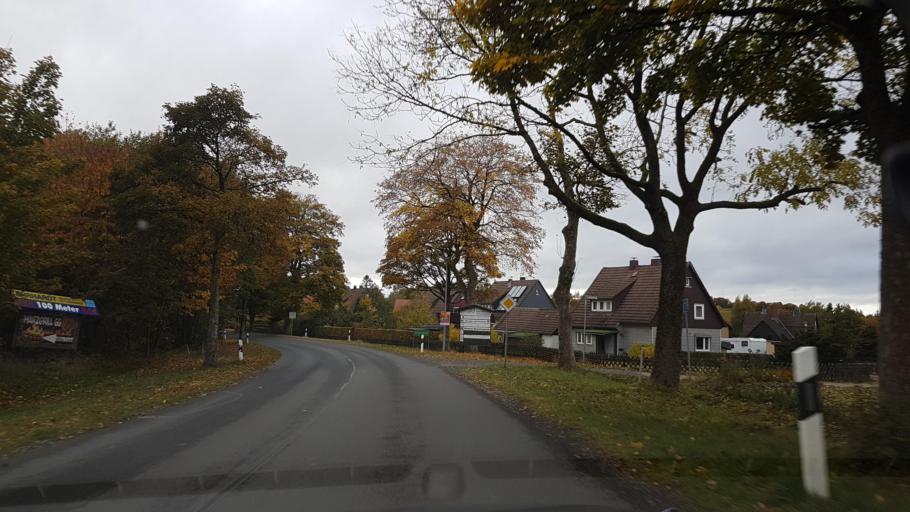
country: DE
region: Lower Saxony
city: Clausthal-Zellerfeld
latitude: 51.8215
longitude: 10.3457
